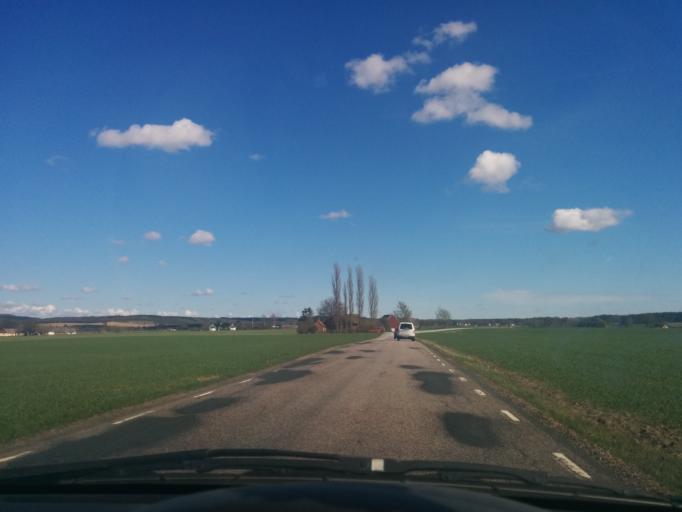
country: SE
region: Skane
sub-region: Lunds Kommun
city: Genarp
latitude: 55.6096
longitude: 13.3623
